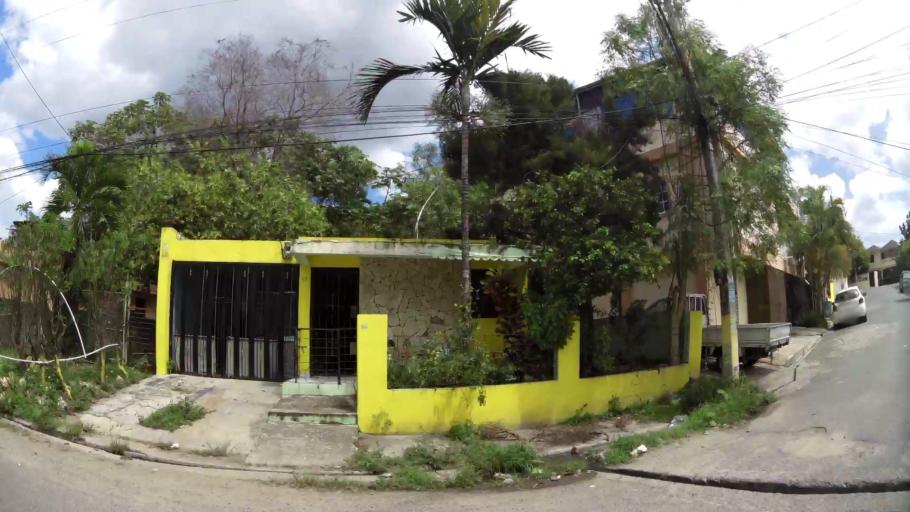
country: DO
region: Nacional
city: Ensanche Luperon
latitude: 18.5268
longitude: -69.9041
